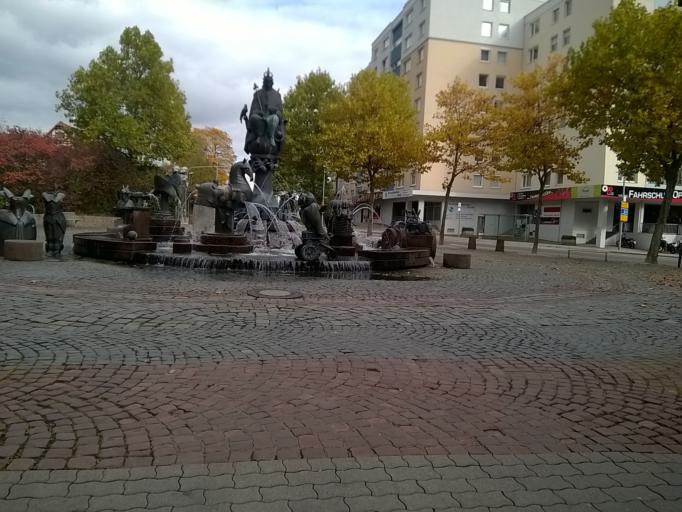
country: DE
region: Rheinland-Pfalz
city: Kaiserslautern
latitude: 49.4480
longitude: 7.7764
